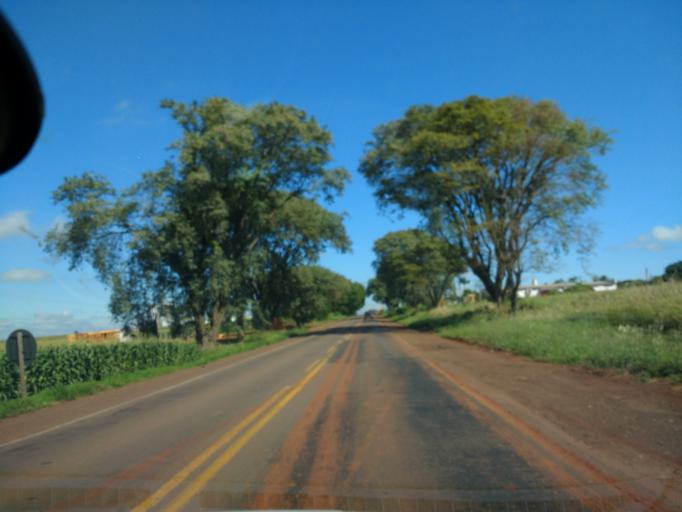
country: BR
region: Parana
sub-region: Terra Boa
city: Terra Boa
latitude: -23.6303
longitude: -52.4584
